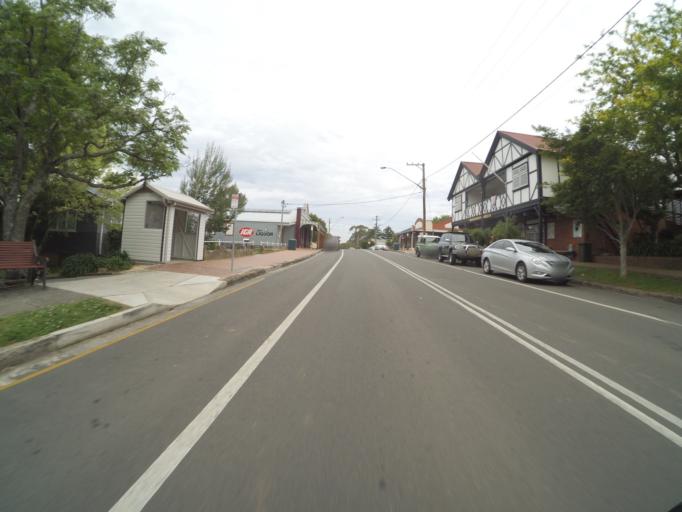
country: AU
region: New South Wales
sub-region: Kiama
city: Jamberoo
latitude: -34.6483
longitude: 150.7752
